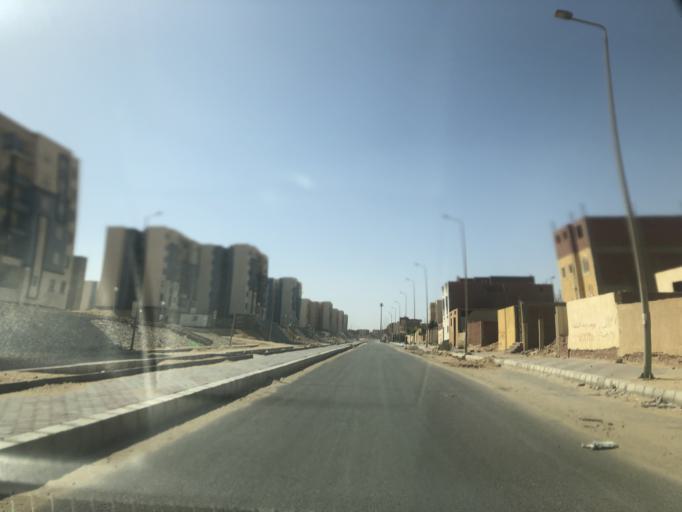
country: EG
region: Al Jizah
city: Madinat Sittah Uktubar
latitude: 29.9324
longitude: 30.9846
